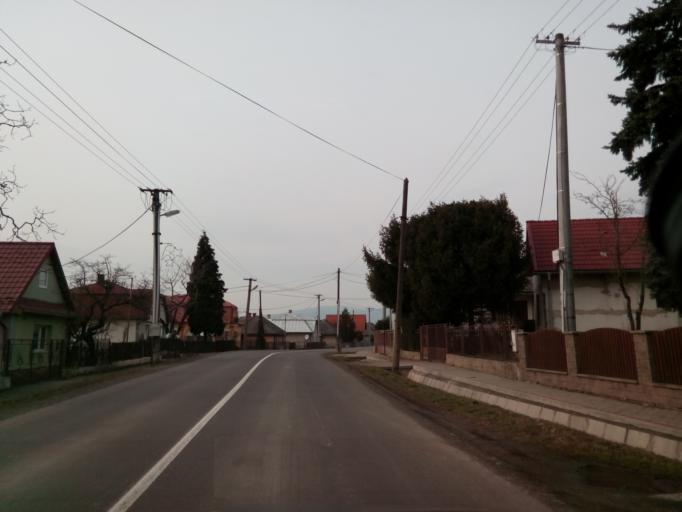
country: SK
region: Kosicky
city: Trebisov
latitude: 48.6046
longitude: 21.6261
